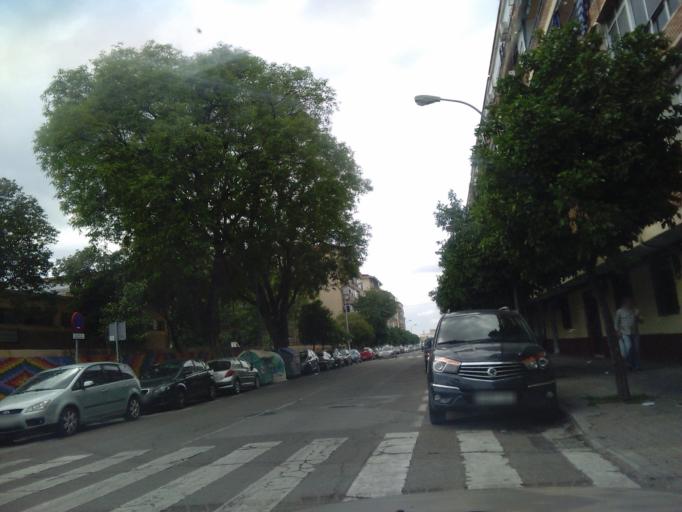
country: ES
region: Andalusia
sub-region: Provincia de Sevilla
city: Sevilla
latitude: 37.4112
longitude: -5.9288
